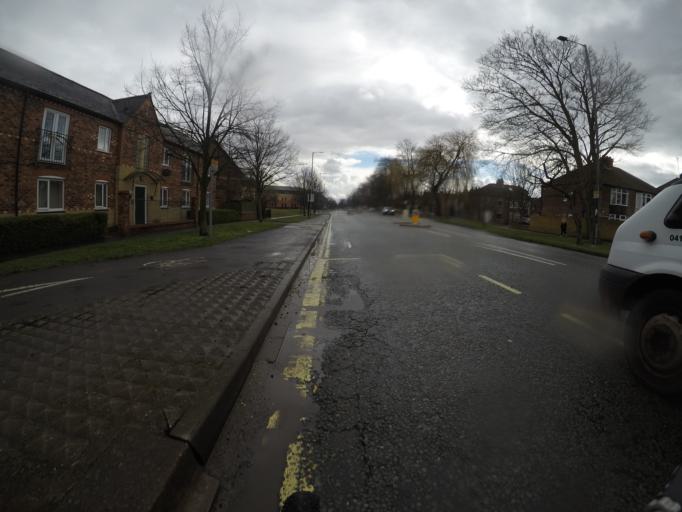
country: GB
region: England
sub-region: City of York
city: York
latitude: 53.9597
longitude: -1.1119
